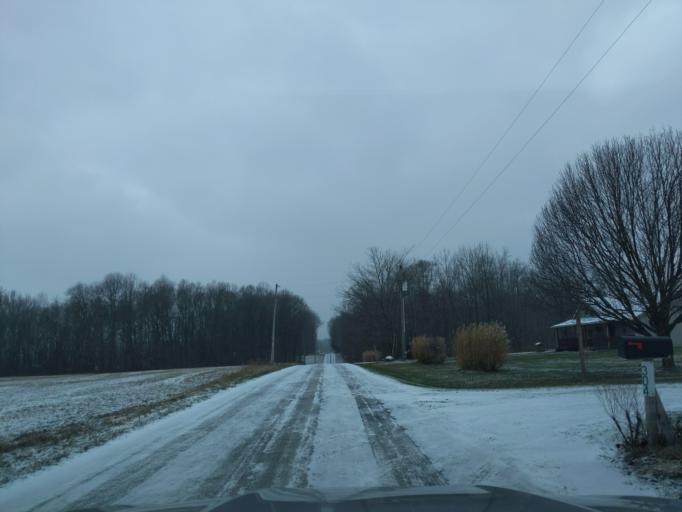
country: US
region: Indiana
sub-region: Decatur County
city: Greensburg
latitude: 39.2341
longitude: -85.4845
